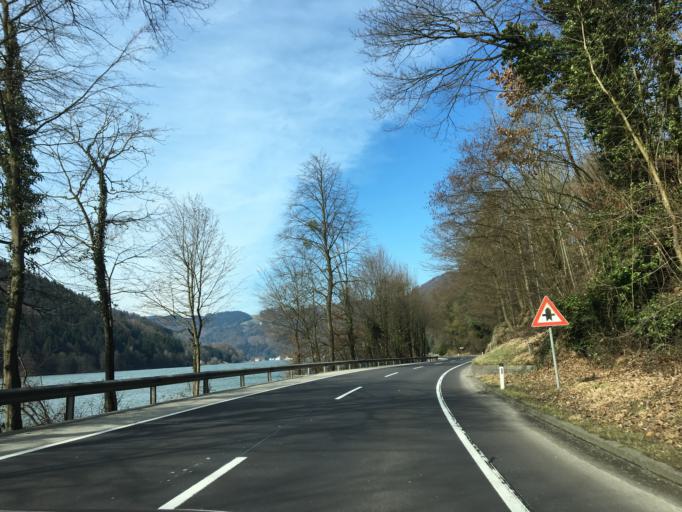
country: AT
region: Lower Austria
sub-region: Politischer Bezirk Melk
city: Nochling
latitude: 48.2118
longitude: 14.9566
